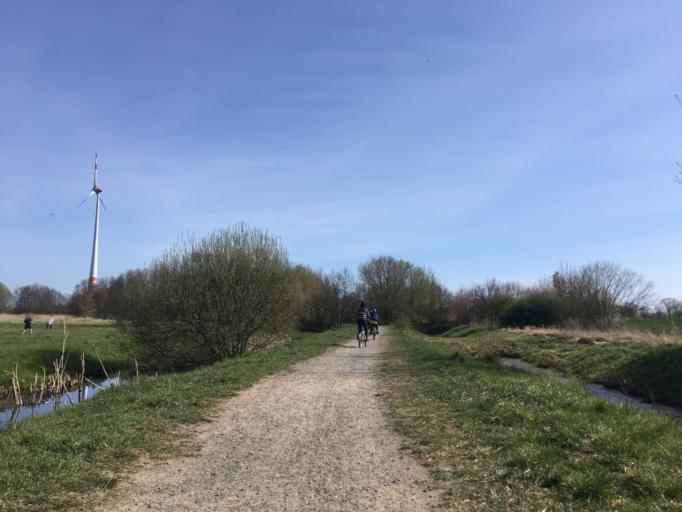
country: DE
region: Berlin
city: Karow
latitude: 52.5999
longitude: 13.4926
